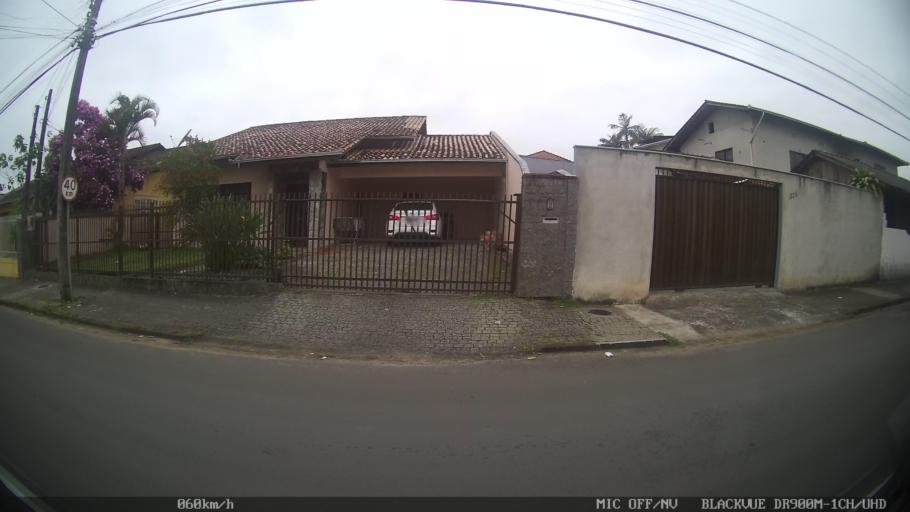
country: BR
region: Santa Catarina
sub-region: Joinville
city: Joinville
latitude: -26.3215
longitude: -48.8302
